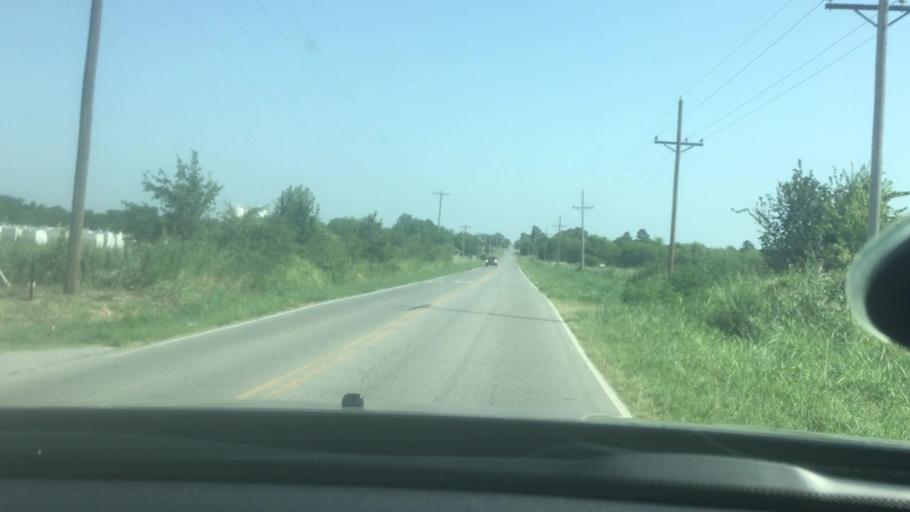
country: US
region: Oklahoma
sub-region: Bryan County
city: Calera
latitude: 33.9996
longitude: -96.4656
